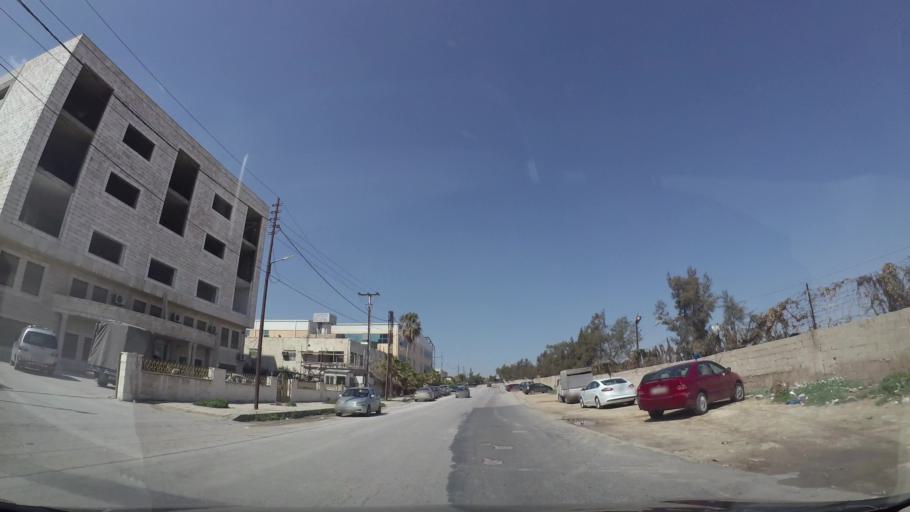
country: JO
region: Zarqa
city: Russeifa
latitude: 31.9940
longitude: 36.0118
